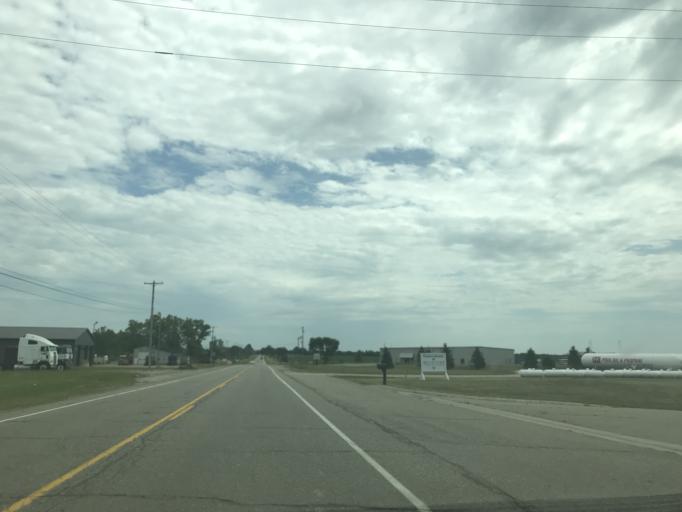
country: US
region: Michigan
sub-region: Eaton County
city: Grand Ledge
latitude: 42.7975
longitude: -84.7371
